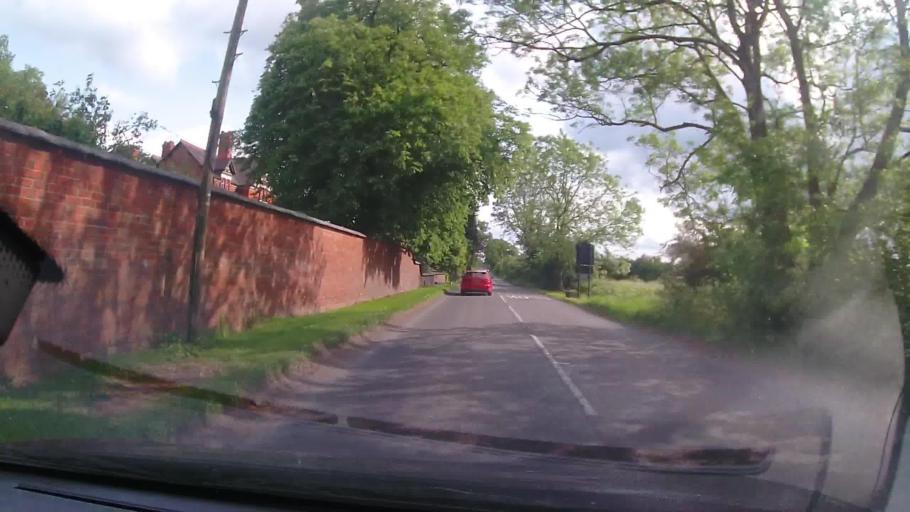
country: GB
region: England
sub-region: Shropshire
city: Wem
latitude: 52.8470
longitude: -2.7287
